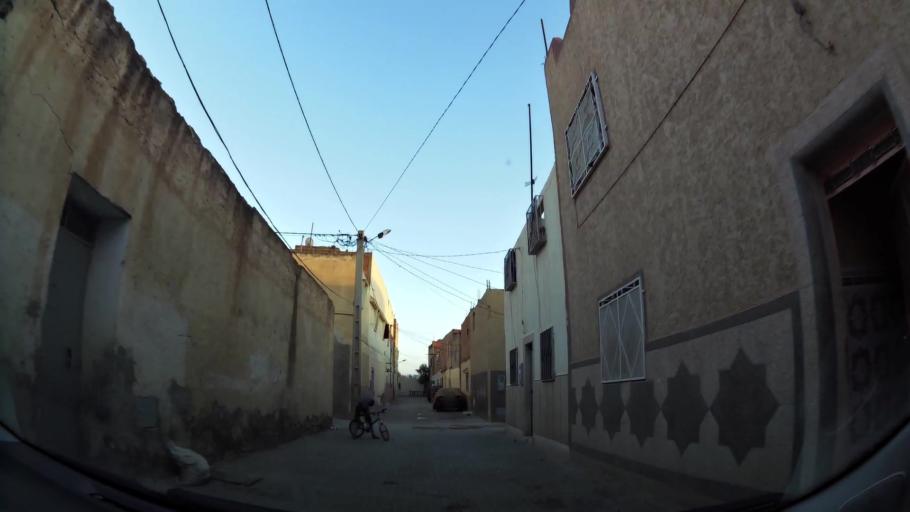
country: MA
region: Oriental
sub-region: Oujda-Angad
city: Oujda
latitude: 34.6995
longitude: -1.9243
